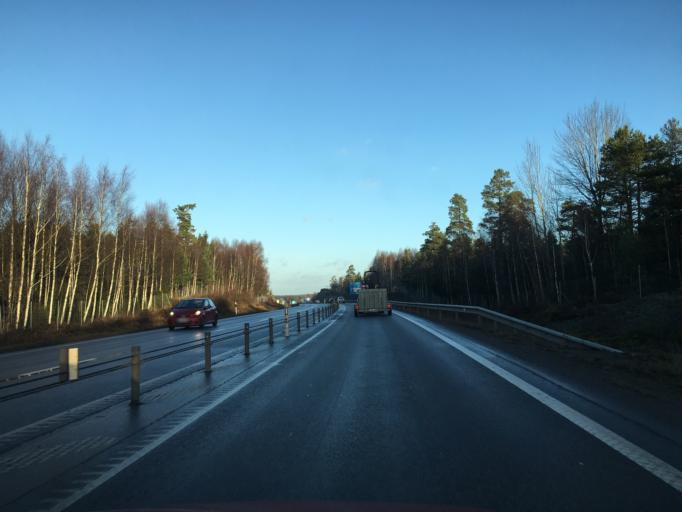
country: SE
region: Kalmar
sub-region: Vasterviks Kommun
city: Vaestervik
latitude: 57.7473
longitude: 16.5578
